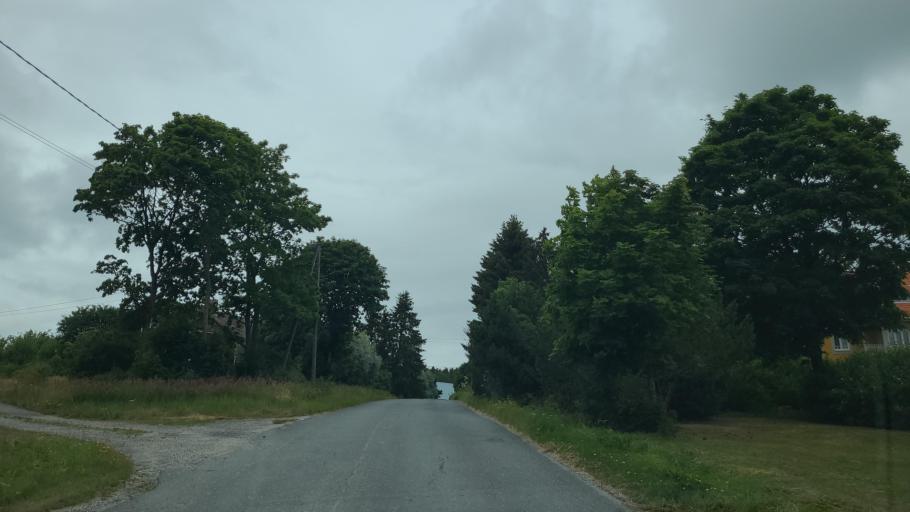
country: FI
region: Varsinais-Suomi
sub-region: Aboland-Turunmaa
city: Dragsfjaerd
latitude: 60.0731
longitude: 22.4519
